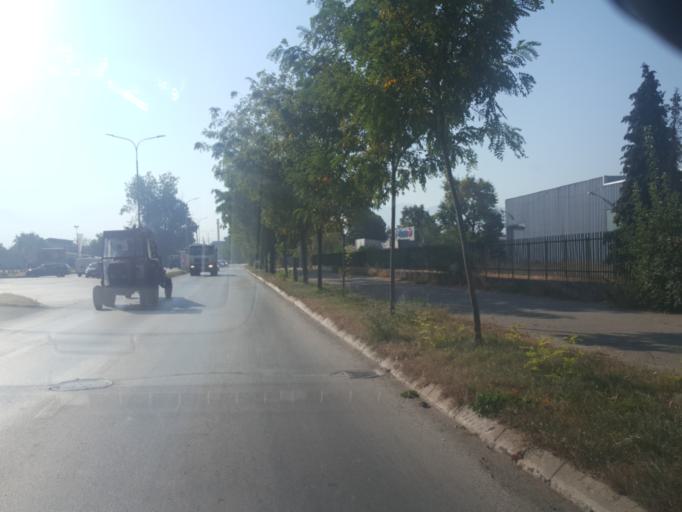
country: XK
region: Gjakova
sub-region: Komuna e Gjakoves
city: Gjakove
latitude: 42.3949
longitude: 20.4214
